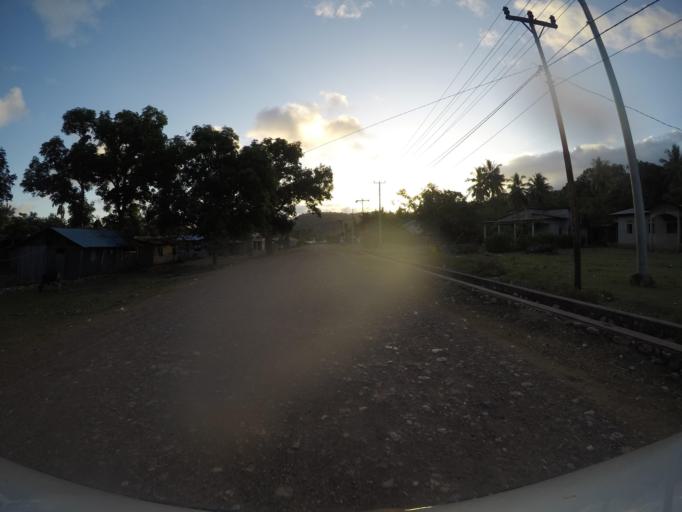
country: TL
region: Baucau
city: Venilale
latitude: -8.7494
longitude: 126.7013
